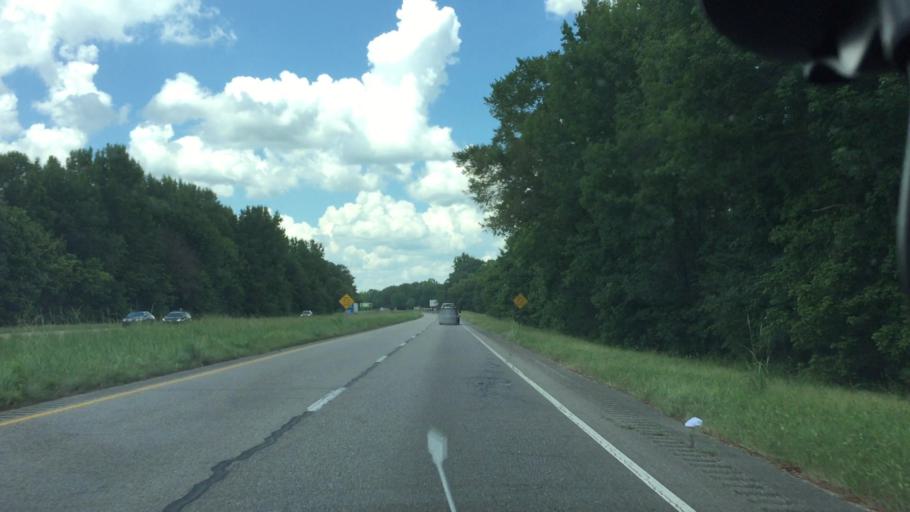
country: US
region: Alabama
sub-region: Montgomery County
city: Pike Road
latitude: 32.1075
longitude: -86.0657
